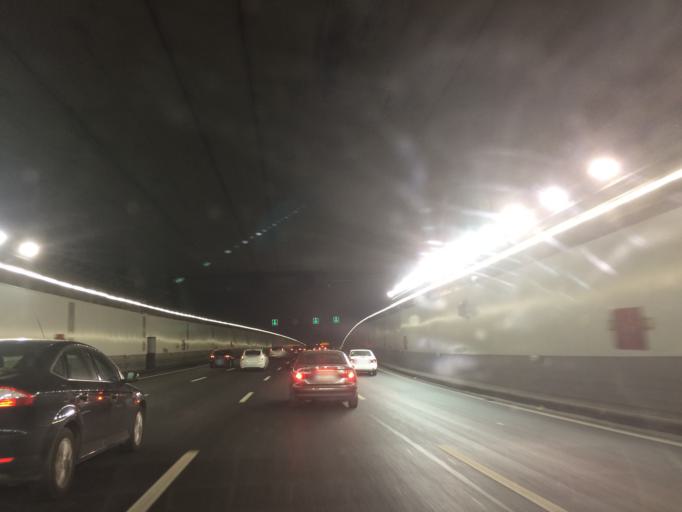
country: ES
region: Madrid
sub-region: Provincia de Madrid
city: Latina
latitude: 40.4111
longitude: -3.7386
